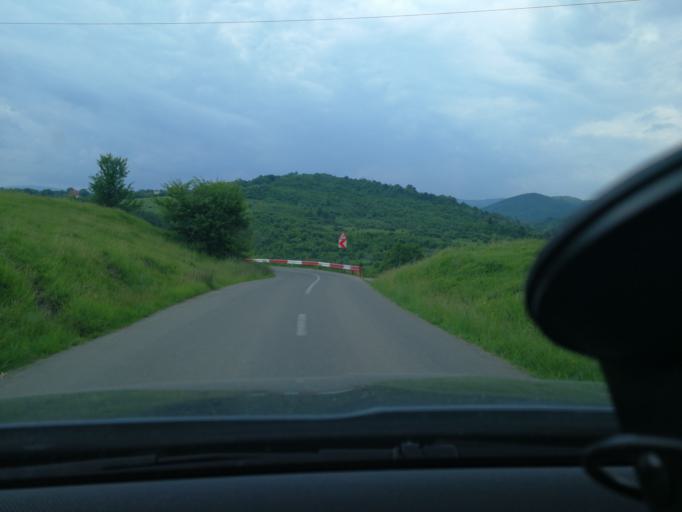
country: RO
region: Prahova
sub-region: Municipiul Campina
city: Campina
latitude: 45.1463
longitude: 25.7313
